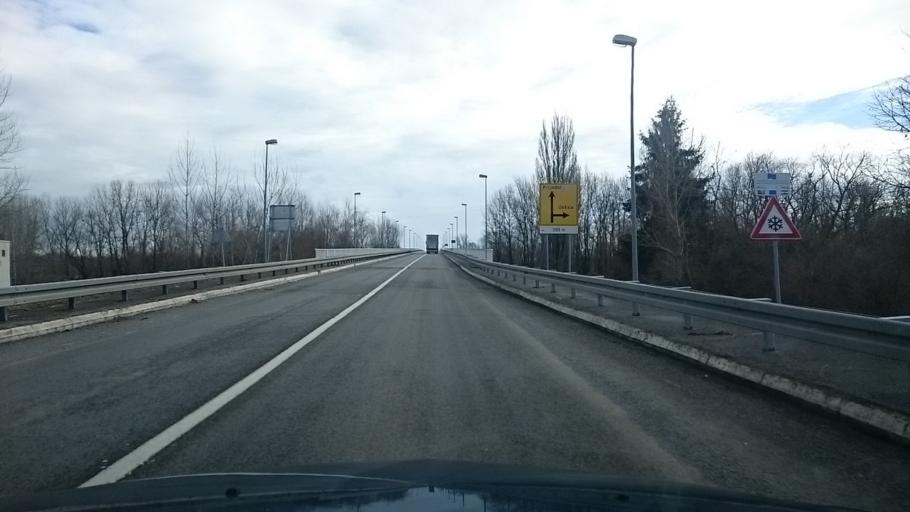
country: HR
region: Sisacko-Moslavacka
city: Novska
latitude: 45.2704
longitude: 16.9122
